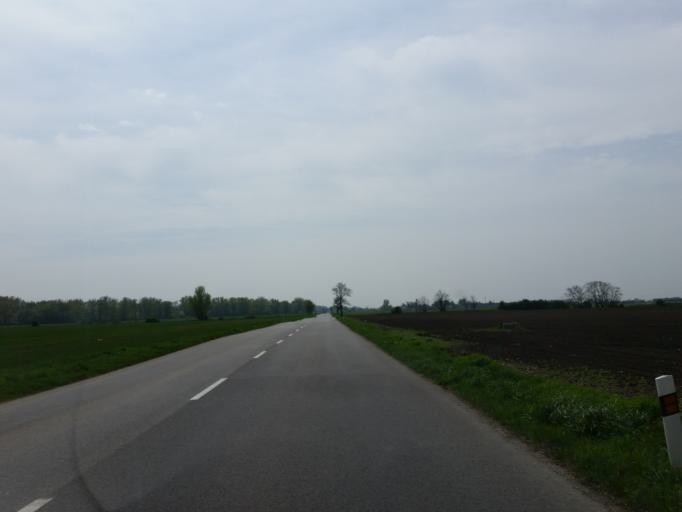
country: SK
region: Trnavsky
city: Leopoldov
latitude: 48.4140
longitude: 17.7635
